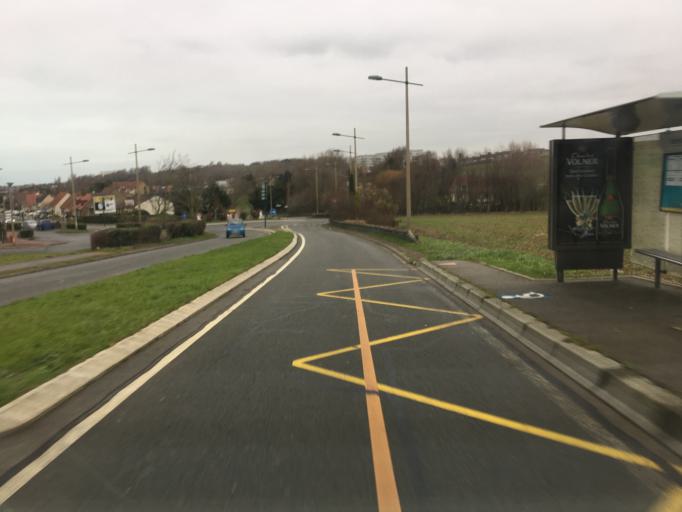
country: FR
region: Nord-Pas-de-Calais
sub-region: Departement du Pas-de-Calais
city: Le Portel
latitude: 50.6939
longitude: 1.5784
